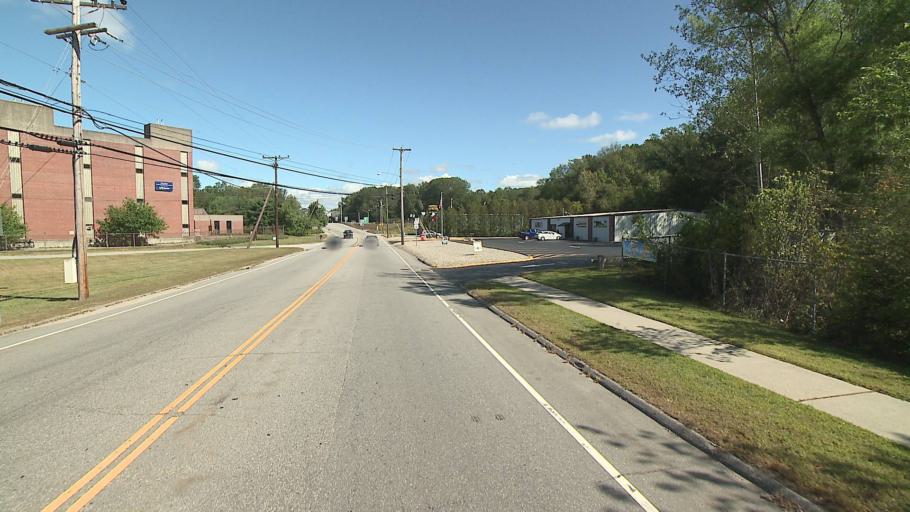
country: US
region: Connecticut
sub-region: Windham County
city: Danielson
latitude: 41.7941
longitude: -71.8848
